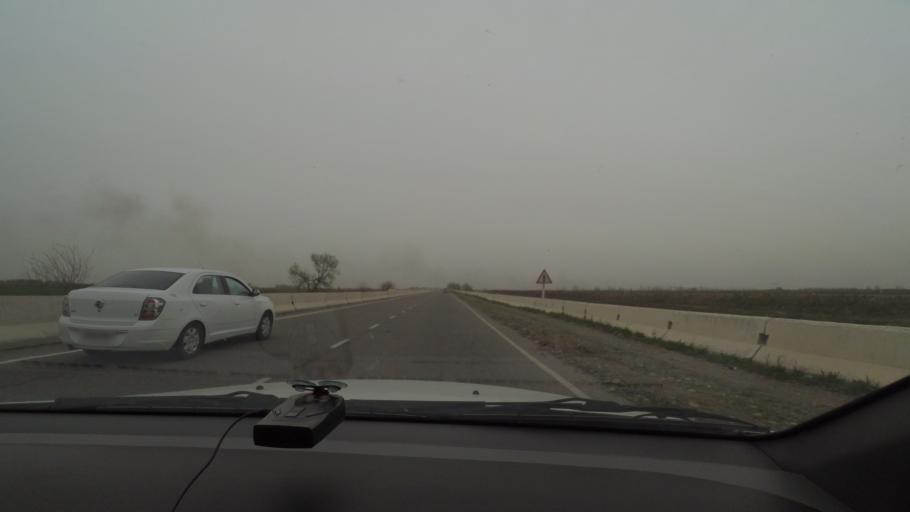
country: UZ
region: Jizzax
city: Gagarin
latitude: 40.5125
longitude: 68.3233
